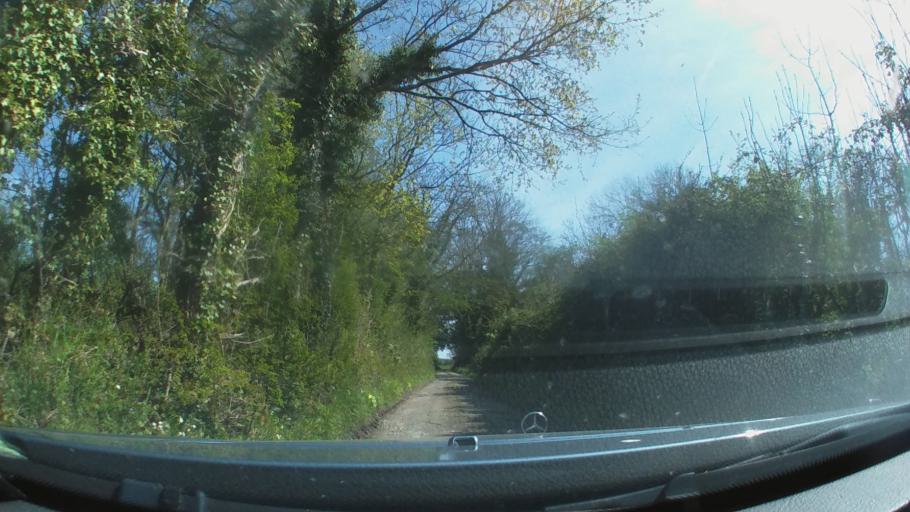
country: IE
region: Leinster
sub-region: Kilkenny
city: Callan
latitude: 52.6007
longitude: -7.3911
